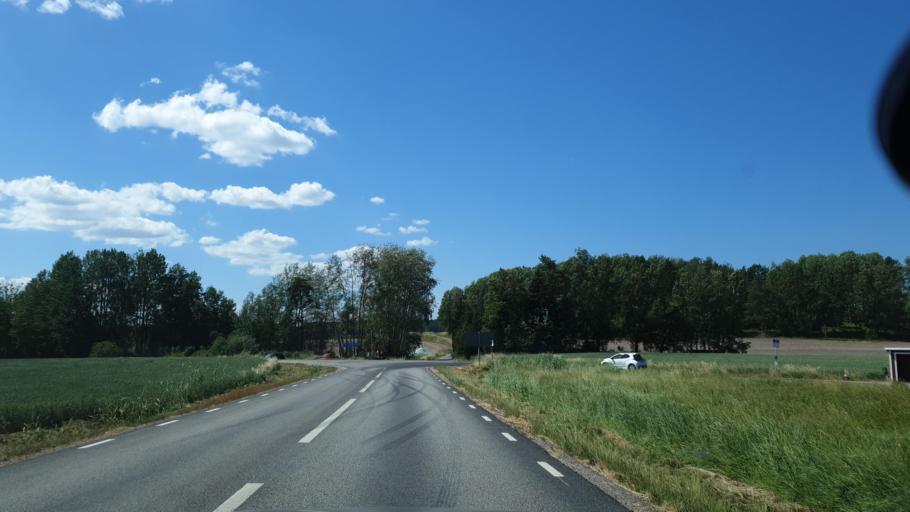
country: SE
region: Stockholm
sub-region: Nykvarns Kommun
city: Nykvarn
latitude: 59.2532
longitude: 17.4491
